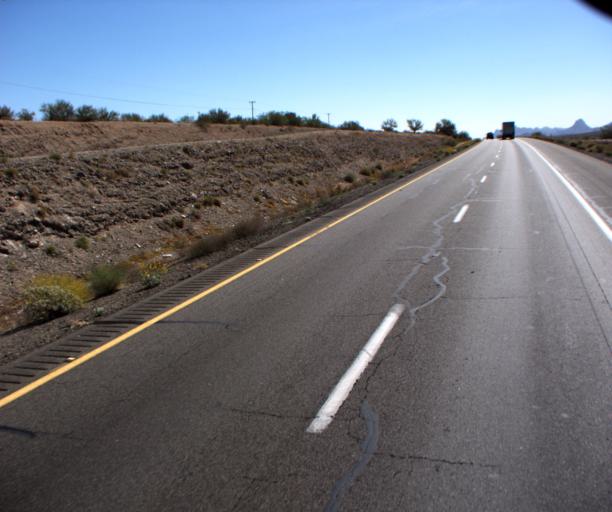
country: US
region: Arizona
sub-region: La Paz County
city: Quartzsite
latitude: 33.6680
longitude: -114.0400
